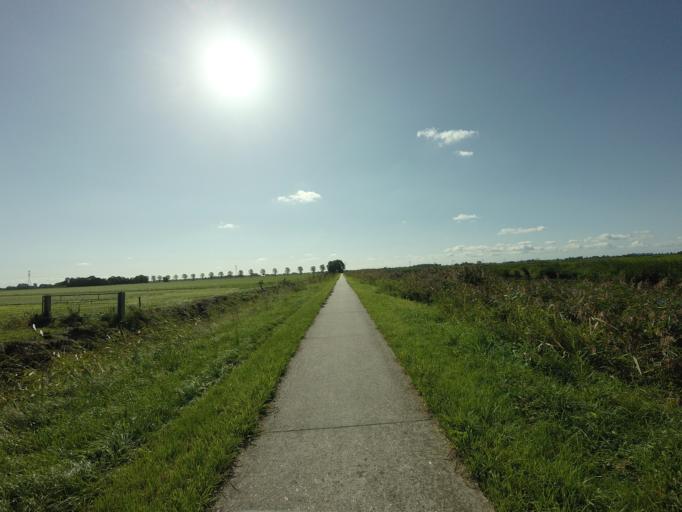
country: NL
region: Friesland
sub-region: Gemeente Boarnsterhim
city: Reduzum
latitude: 53.1235
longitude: 5.7551
